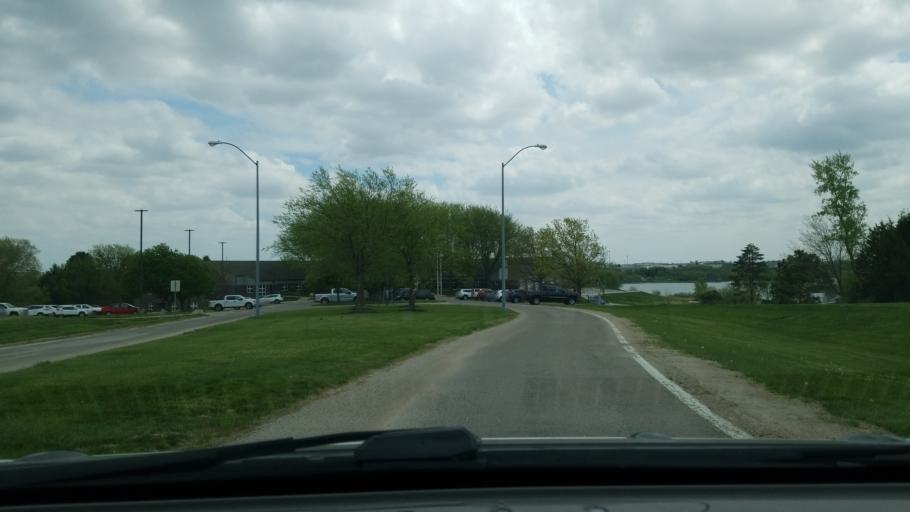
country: US
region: Nebraska
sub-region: Sarpy County
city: Chalco
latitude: 41.1720
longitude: -96.1569
